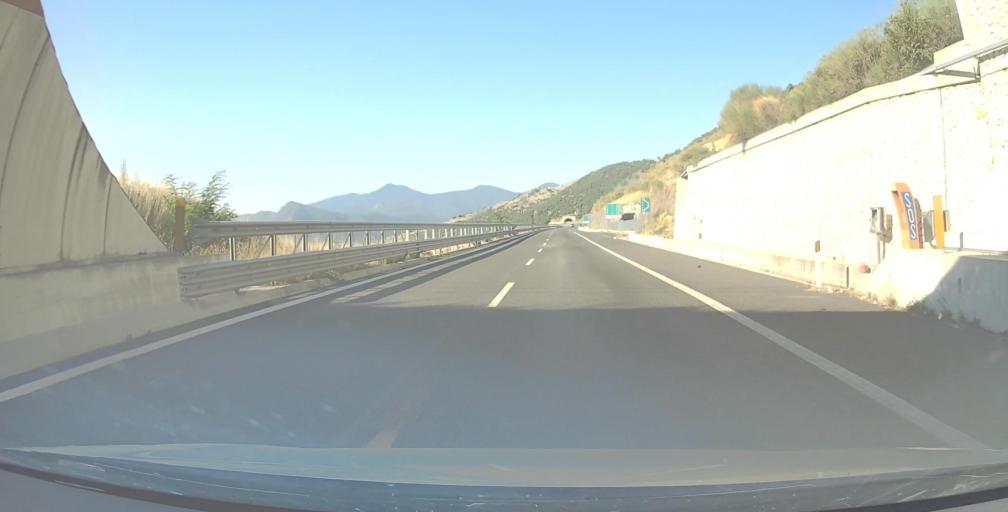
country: IT
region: Calabria
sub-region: Provincia di Cosenza
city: Morano Calabro
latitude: 39.8843
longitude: 16.1341
